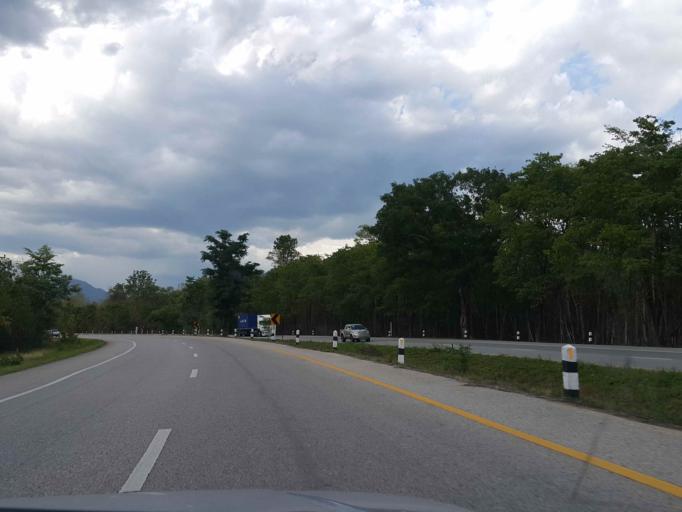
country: TH
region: Lampang
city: Thoen
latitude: 17.7385
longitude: 99.2335
